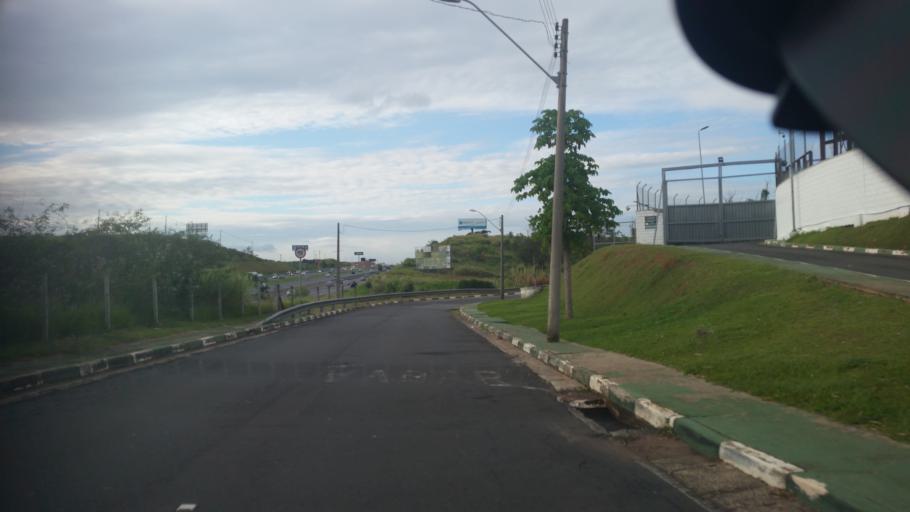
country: BR
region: Sao Paulo
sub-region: Campinas
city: Campinas
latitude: -22.8834
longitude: -47.0129
